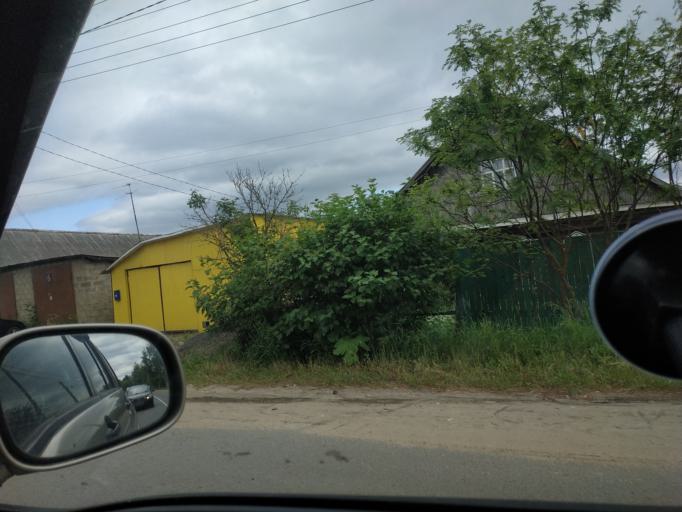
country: RU
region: Moskovskaya
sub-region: Shchelkovskiy Rayon
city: Grebnevo
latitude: 55.9938
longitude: 38.1281
